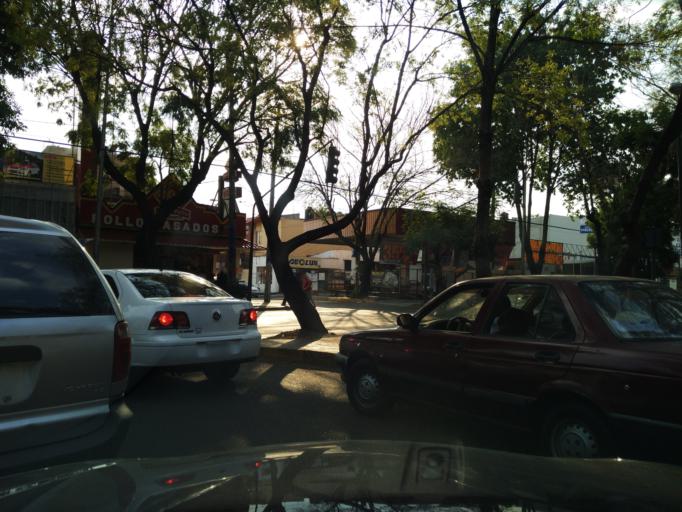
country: MX
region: Mexico City
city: Coyoacan
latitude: 19.3180
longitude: -99.1292
